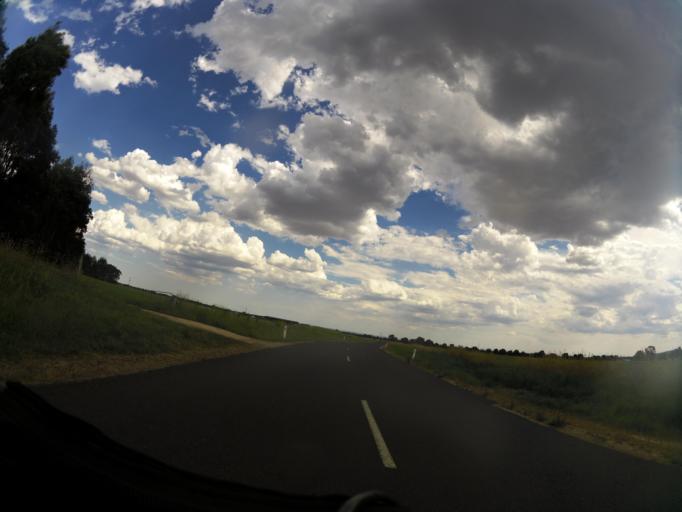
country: AU
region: Victoria
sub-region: Wellington
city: Heyfield
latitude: -37.9877
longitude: 146.6933
